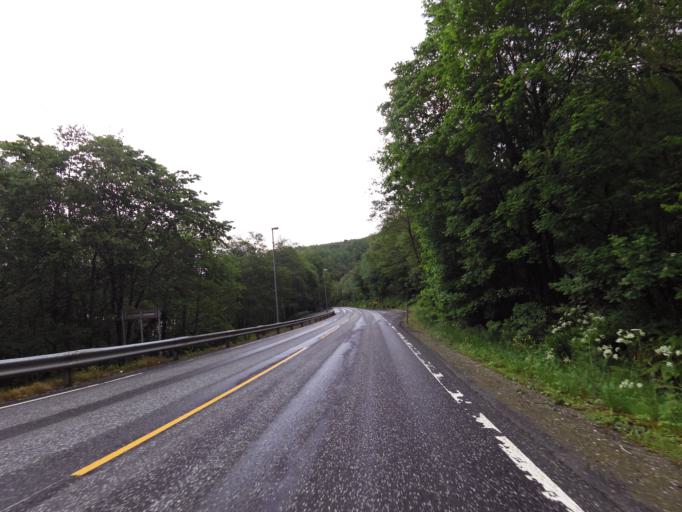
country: NO
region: Vest-Agder
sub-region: Farsund
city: Farsund
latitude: 58.1022
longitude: 6.8988
